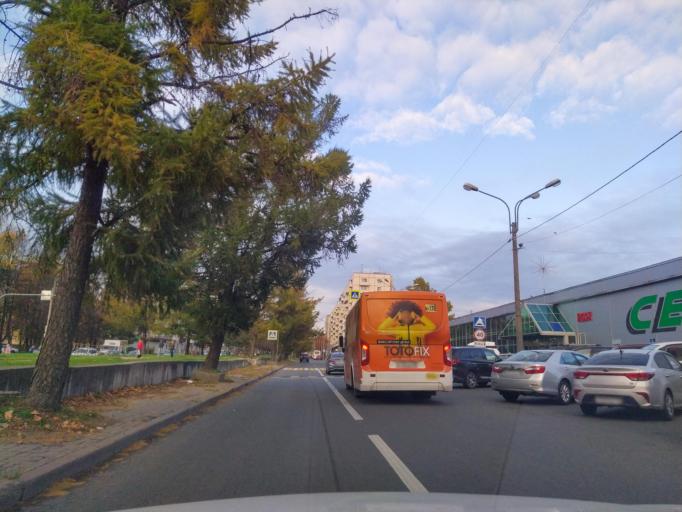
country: RU
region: Leningrad
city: Kalininskiy
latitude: 59.9795
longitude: 30.4059
